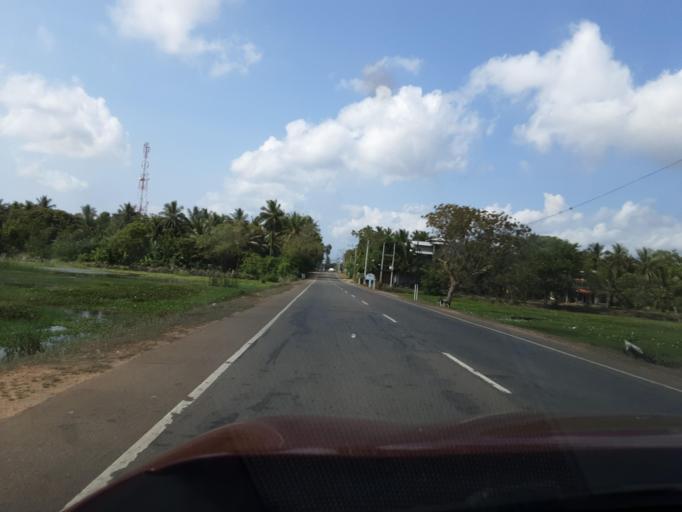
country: LK
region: Southern
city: Tangalla
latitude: 6.2938
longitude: 81.2357
